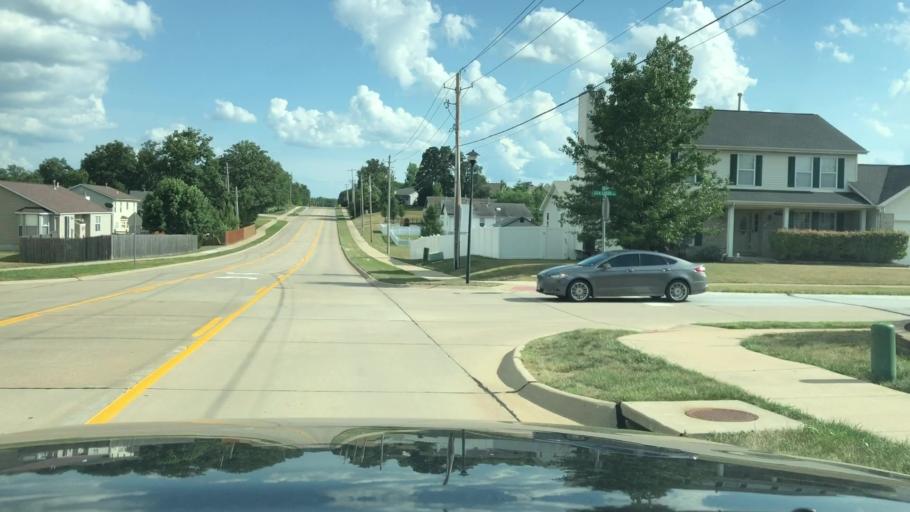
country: US
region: Missouri
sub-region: Saint Charles County
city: Wentzville
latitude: 38.8343
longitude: -90.8922
